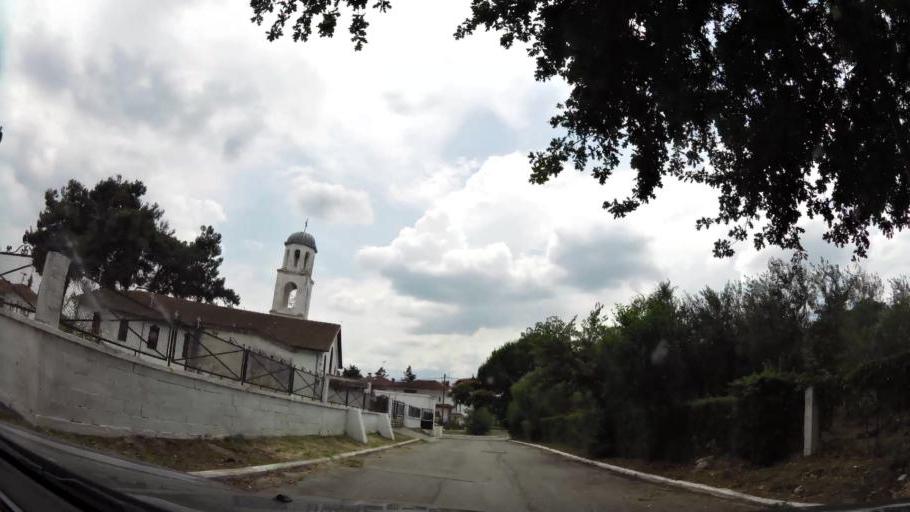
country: GR
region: Central Macedonia
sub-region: Nomos Pierias
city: Kallithea
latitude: 40.2773
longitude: 22.5786
